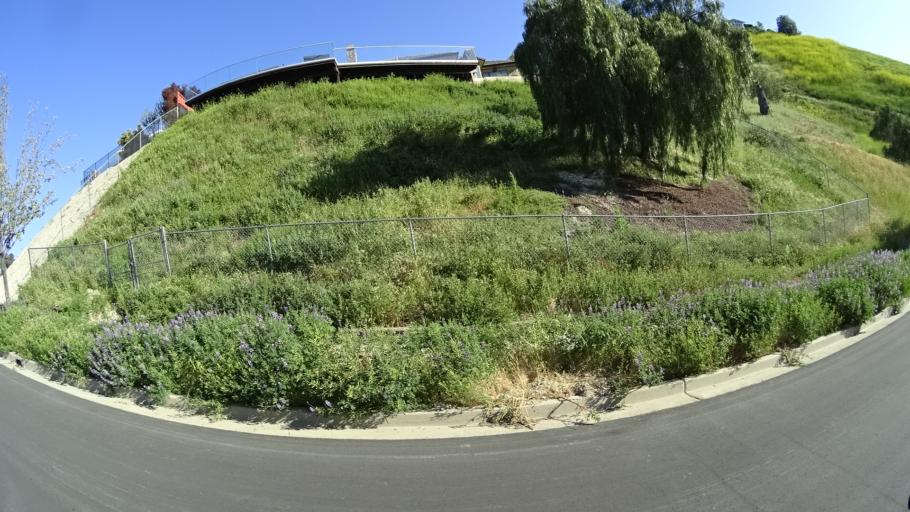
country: US
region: California
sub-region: Ventura County
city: Thousand Oaks
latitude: 34.1914
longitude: -118.8363
